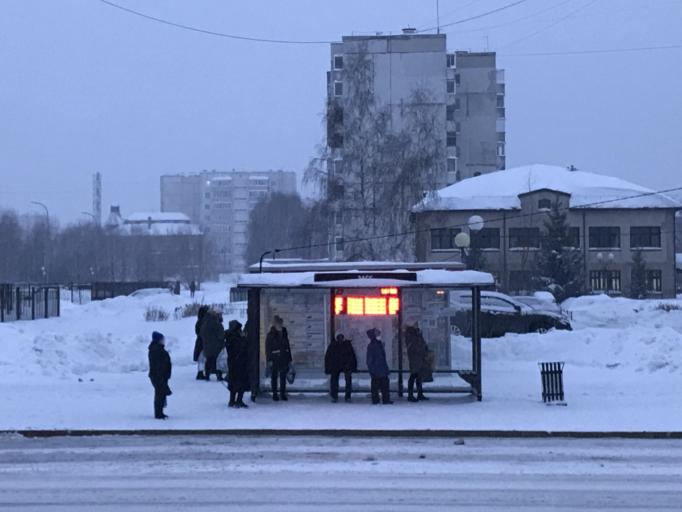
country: RU
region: Tjumen
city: Tobol'sk
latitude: 58.2343
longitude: 68.2720
